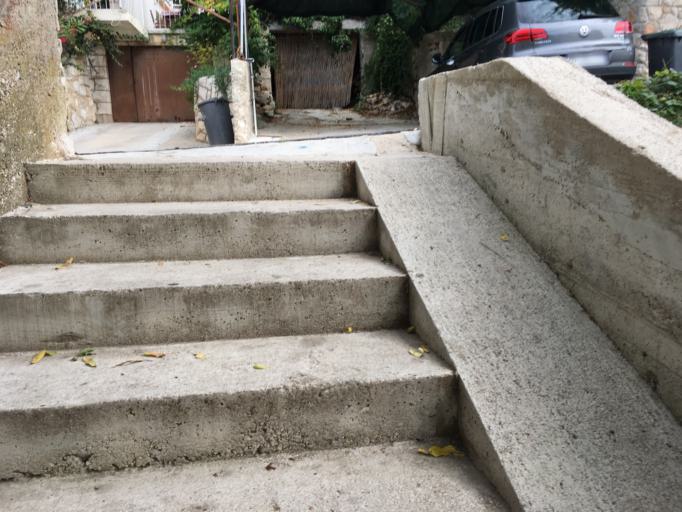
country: HR
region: Splitsko-Dalmatinska
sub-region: Grad Hvar
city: Hvar
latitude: 43.1670
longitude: 16.4473
